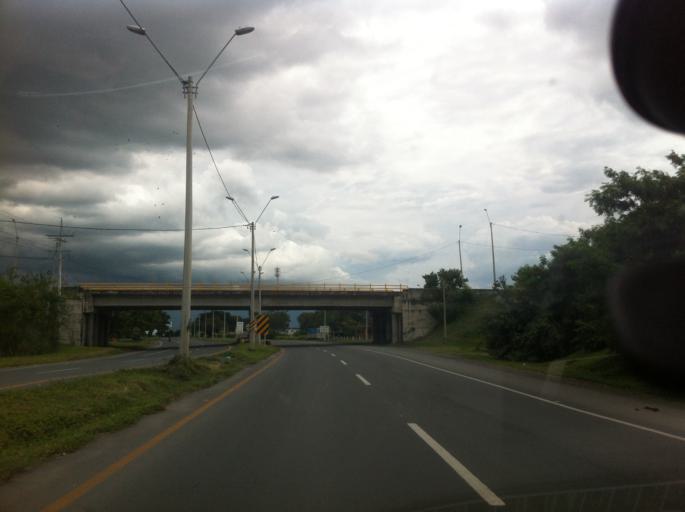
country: CO
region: Valle del Cauca
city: El Cerrito
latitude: 3.7022
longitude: -76.3190
